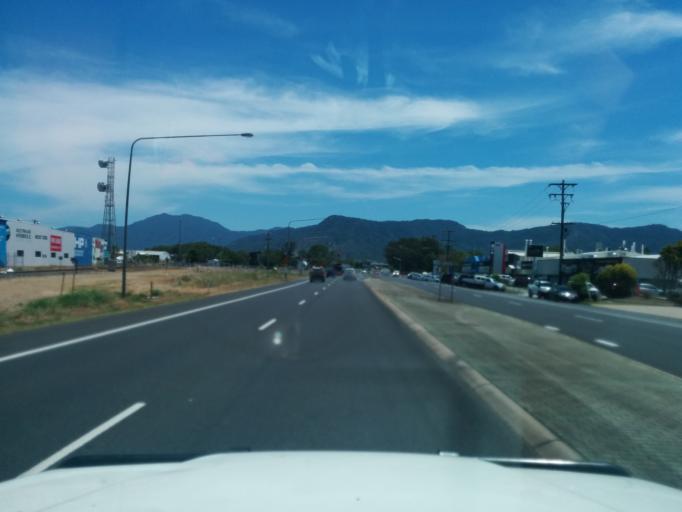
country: AU
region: Queensland
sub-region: Cairns
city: Cairns
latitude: -16.9403
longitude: 145.7694
